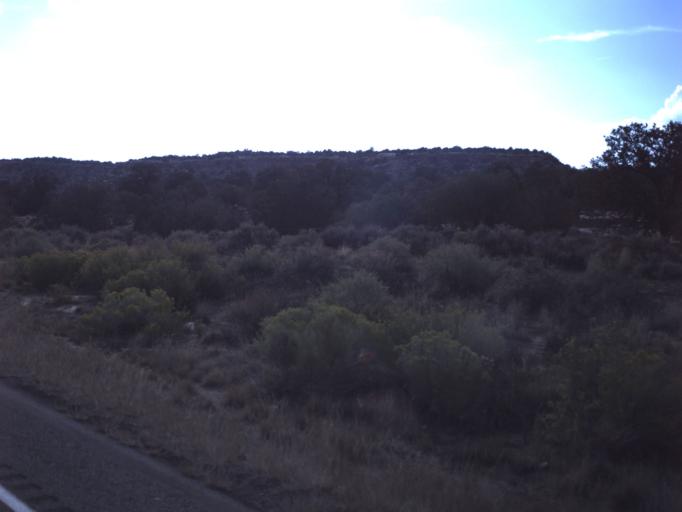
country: US
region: Utah
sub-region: Grand County
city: Moab
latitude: 38.4184
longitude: -109.4365
